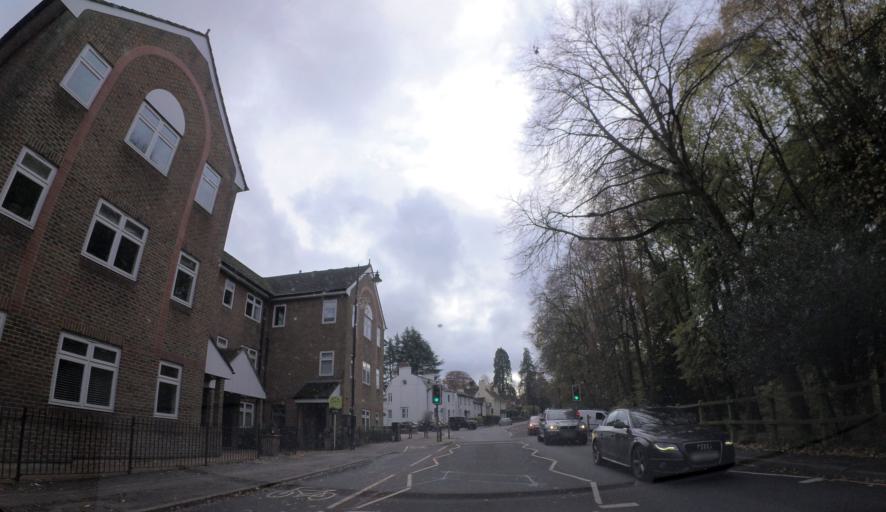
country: GB
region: England
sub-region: Surrey
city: Reigate
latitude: 51.2346
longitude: -0.2039
